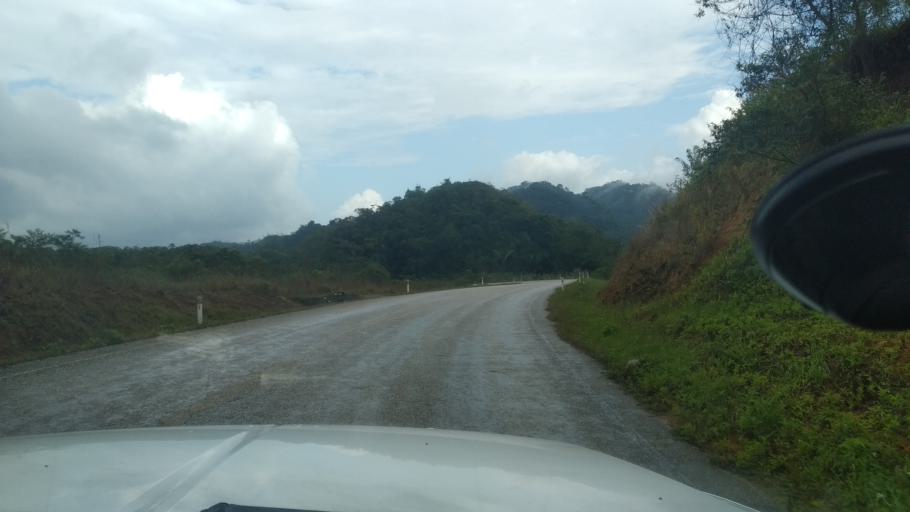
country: GT
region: Peten
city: San Luis
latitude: 16.1885
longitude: -89.1804
